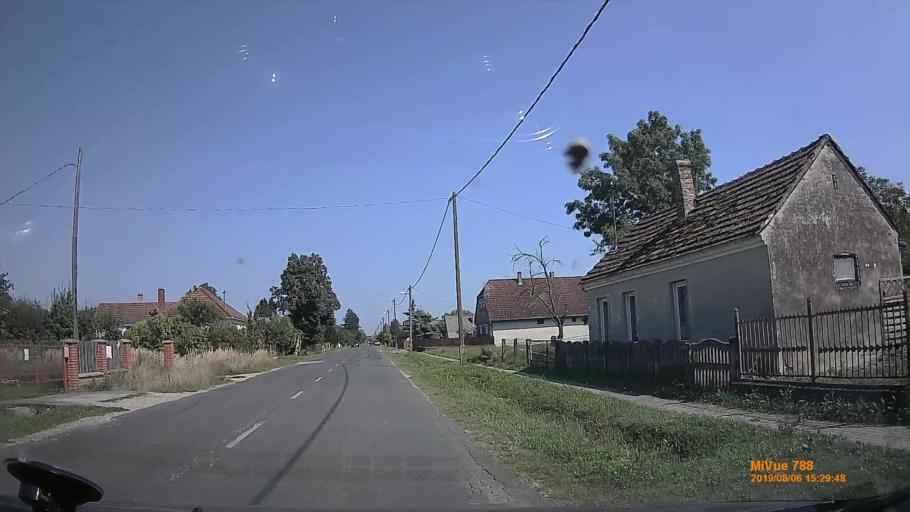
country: HR
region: Koprivnicko-Krizevacka
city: Sigetec
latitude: 46.2404
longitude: 16.9834
